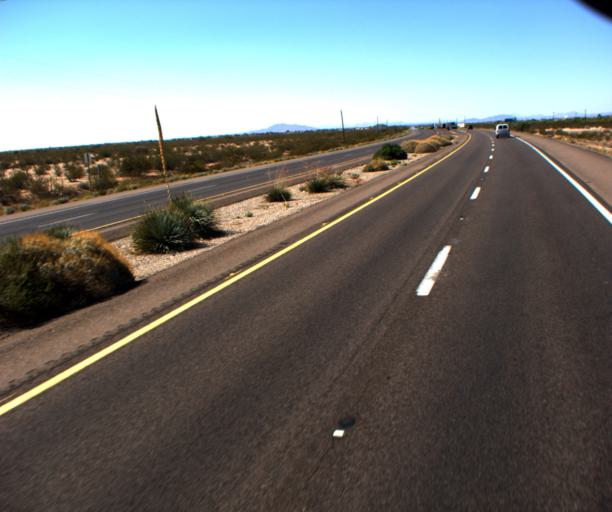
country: US
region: Arizona
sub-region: Pinal County
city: Sacaton
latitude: 32.9955
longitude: -111.7567
